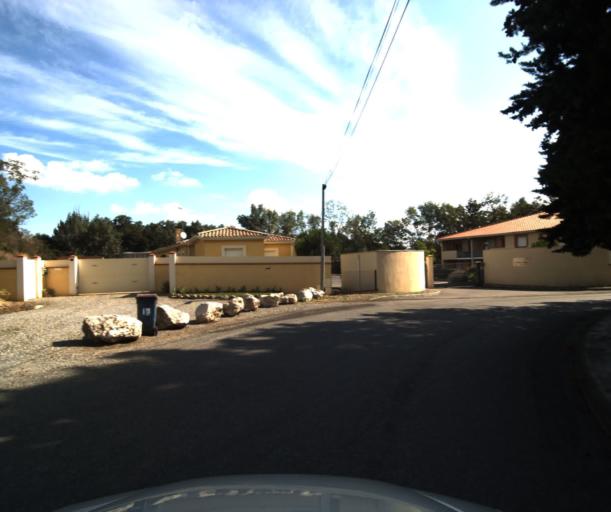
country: FR
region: Midi-Pyrenees
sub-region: Departement de la Haute-Garonne
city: Muret
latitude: 43.4743
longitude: 1.3245
